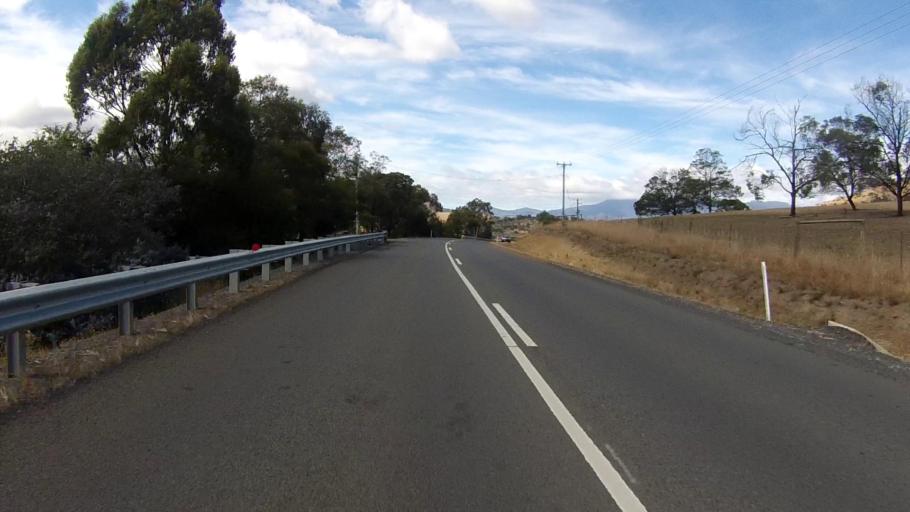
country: AU
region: Tasmania
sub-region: Brighton
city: Old Beach
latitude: -42.7330
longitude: 147.2891
